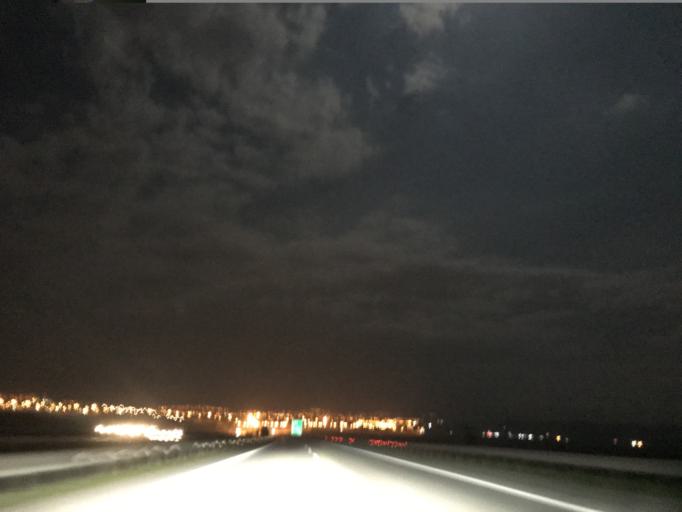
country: TR
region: Hatay
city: Mahmutlar
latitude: 36.9650
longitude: 36.0963
